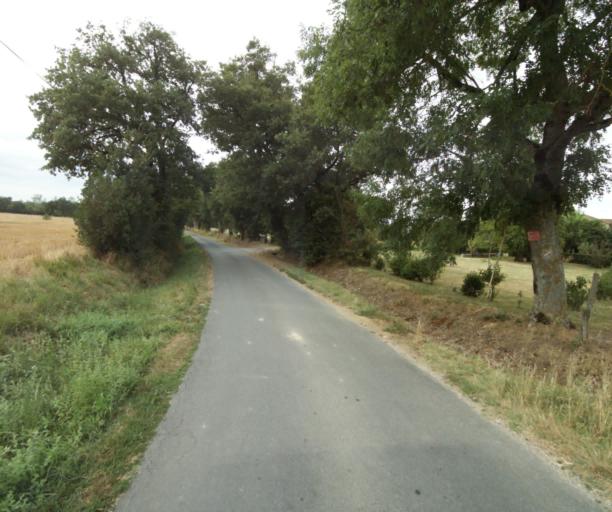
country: FR
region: Midi-Pyrenees
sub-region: Departement du Tarn
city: Soreze
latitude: 43.4607
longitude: 2.0602
